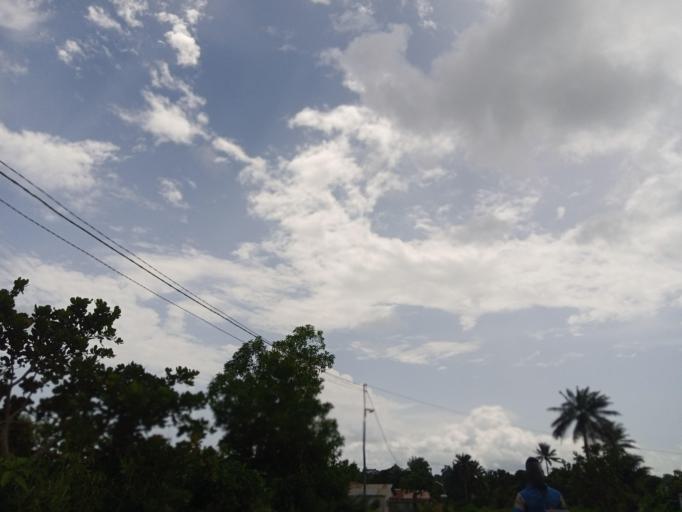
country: SL
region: Northern Province
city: Sawkta
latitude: 8.6333
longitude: -13.2050
